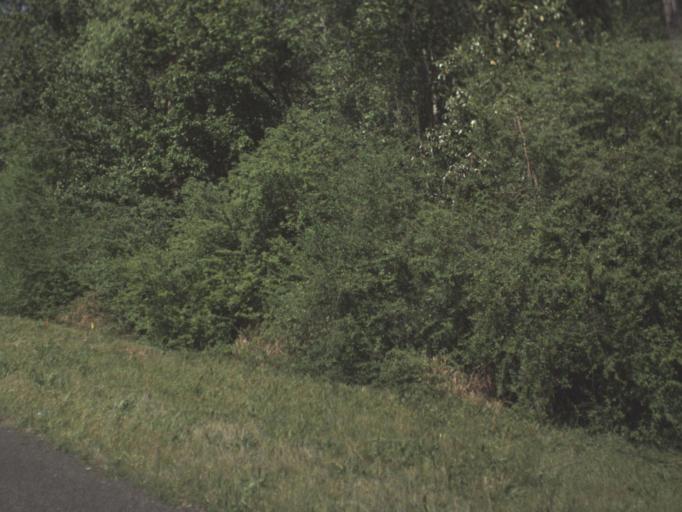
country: US
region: Florida
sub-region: Escambia County
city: Molino
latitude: 30.6912
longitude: -87.3507
